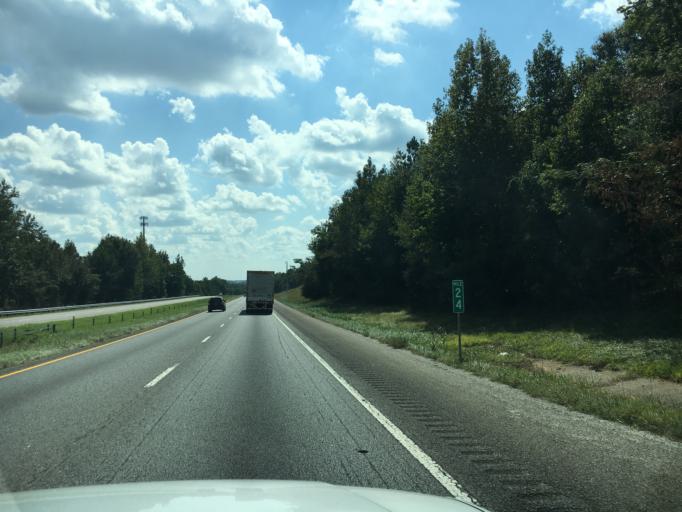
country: US
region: South Carolina
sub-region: Spartanburg County
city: Roebuck
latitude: 34.8944
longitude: -81.9927
